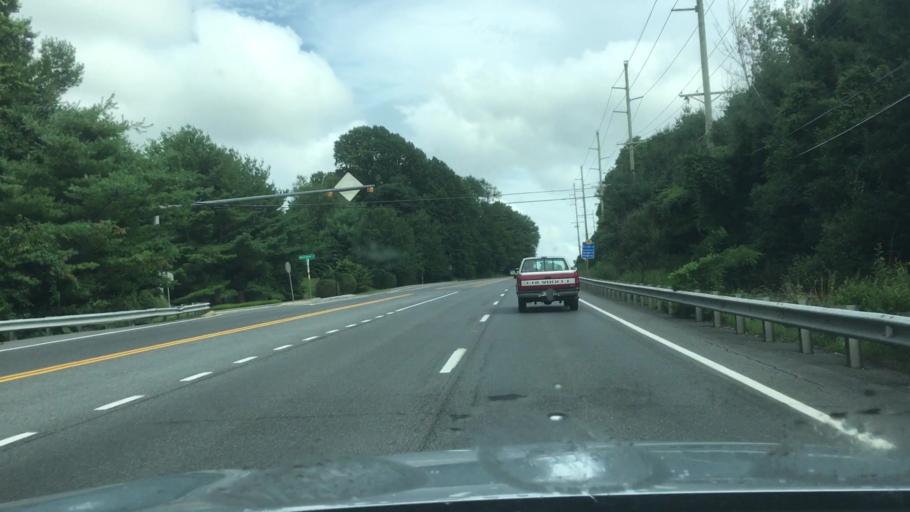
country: US
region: Delaware
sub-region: New Castle County
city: North Star
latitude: 39.7708
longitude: -75.7107
